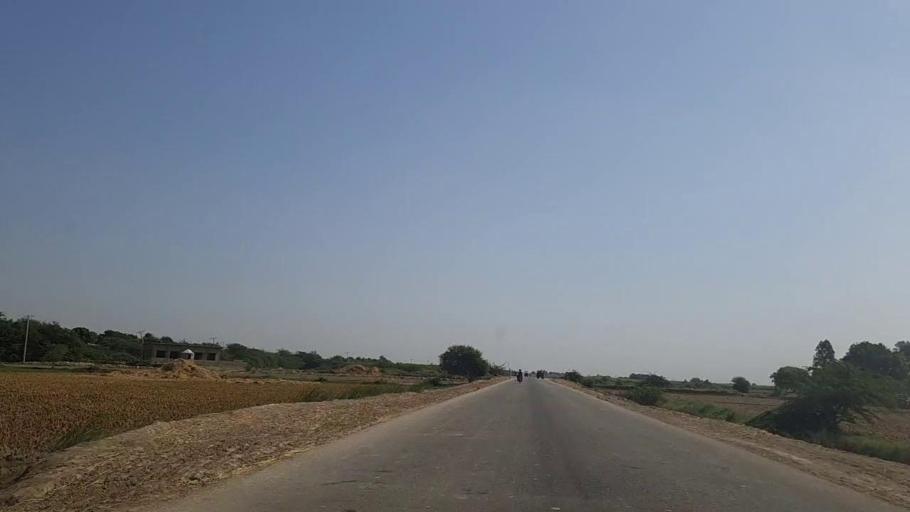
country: PK
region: Sindh
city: Mirpur Batoro
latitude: 24.7567
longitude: 68.2269
